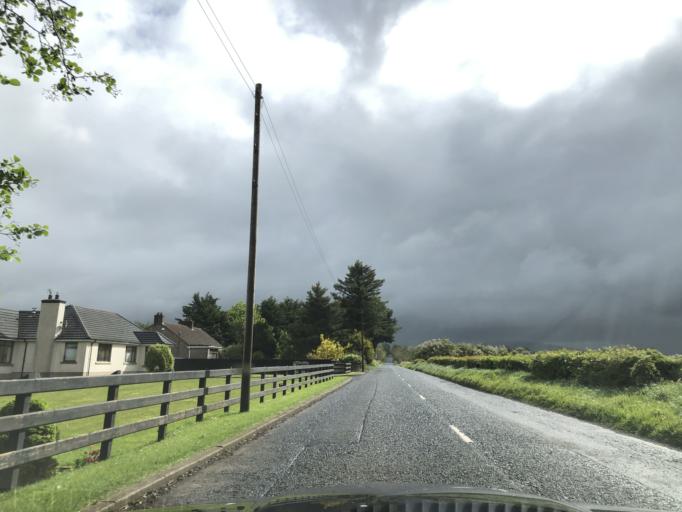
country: GB
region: Northern Ireland
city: Bushmills
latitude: 55.1595
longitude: -6.3889
